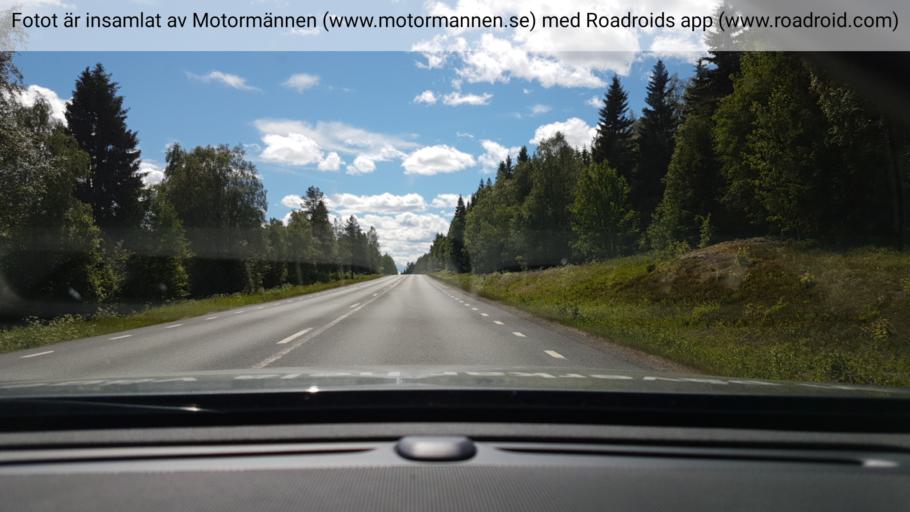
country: SE
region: Vaesterbotten
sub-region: Skelleftea Kommun
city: Burea
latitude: 64.3668
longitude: 21.2998
